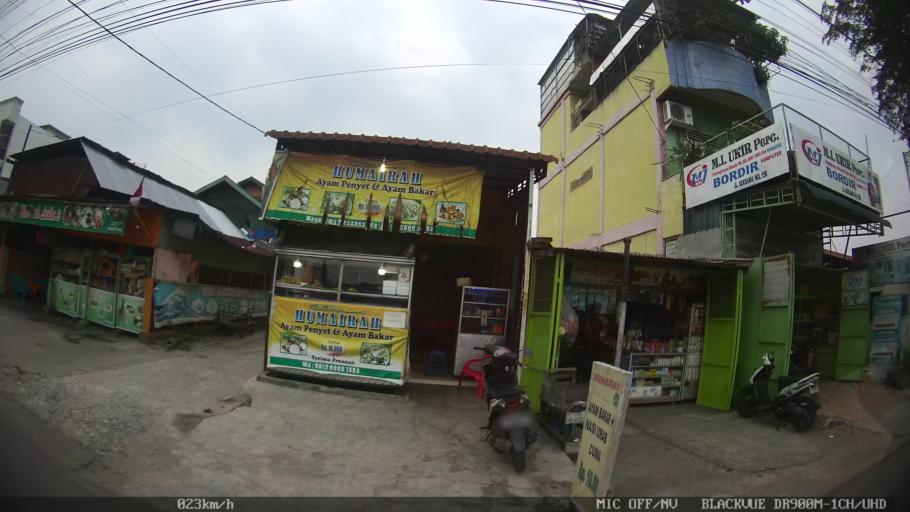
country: ID
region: North Sumatra
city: Deli Tua
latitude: 3.5524
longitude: 98.7104
